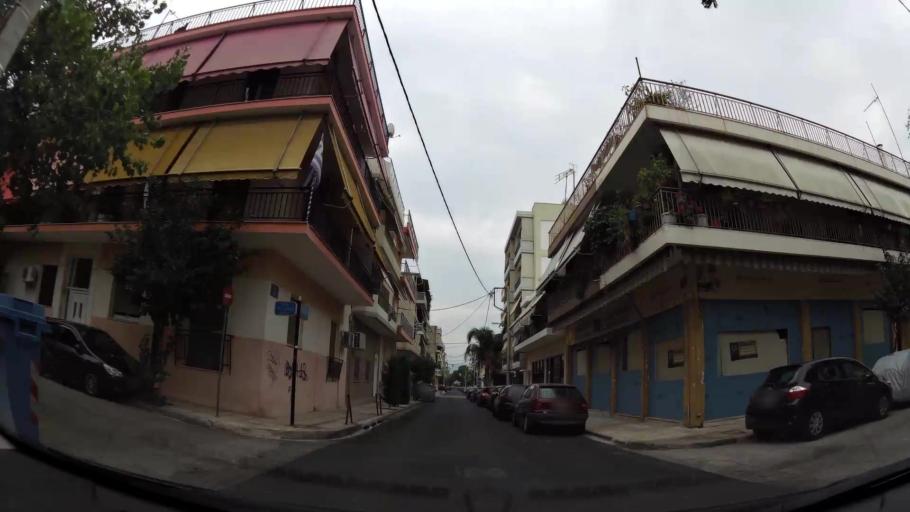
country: GR
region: Attica
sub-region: Nomarchia Athinas
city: Aigaleo
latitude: 37.9963
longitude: 23.6855
